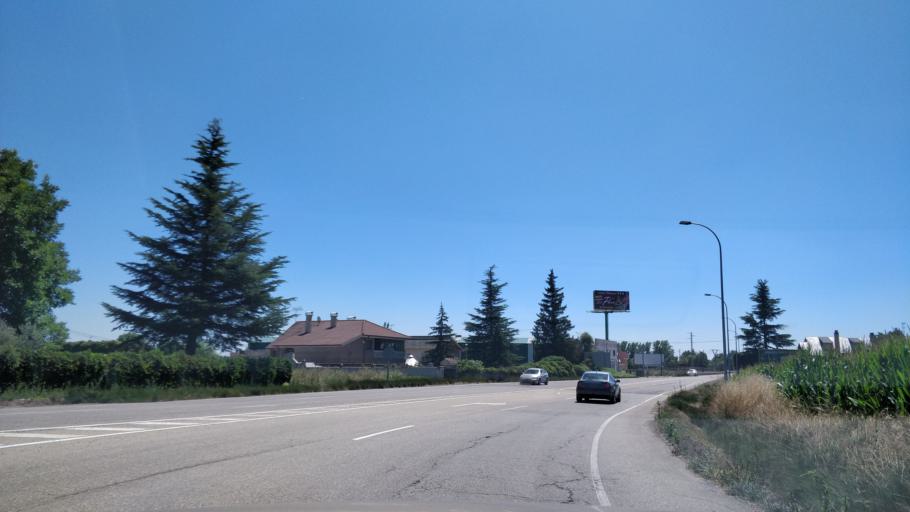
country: ES
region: Castille and Leon
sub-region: Provincia de Leon
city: La Baneza
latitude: 42.3120
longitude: -5.8929
